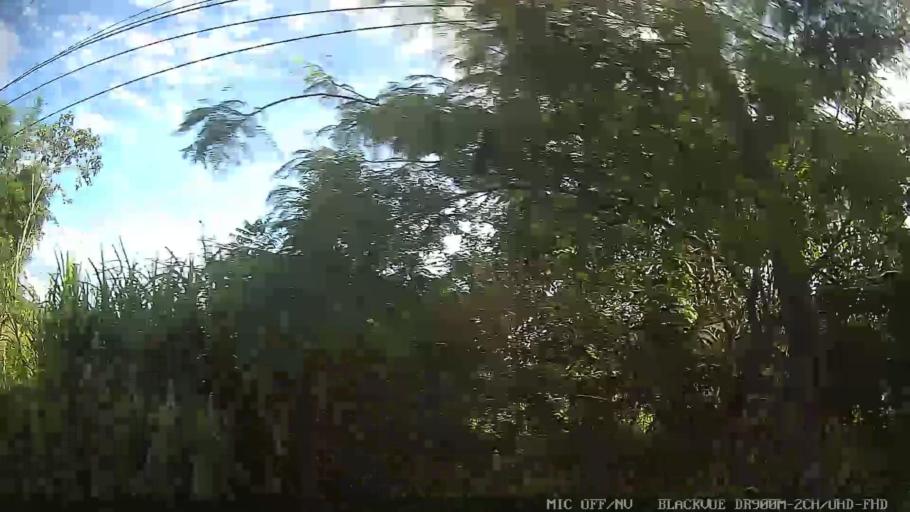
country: BR
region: Sao Paulo
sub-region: Mogi das Cruzes
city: Mogi das Cruzes
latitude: -23.5374
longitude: -46.1564
